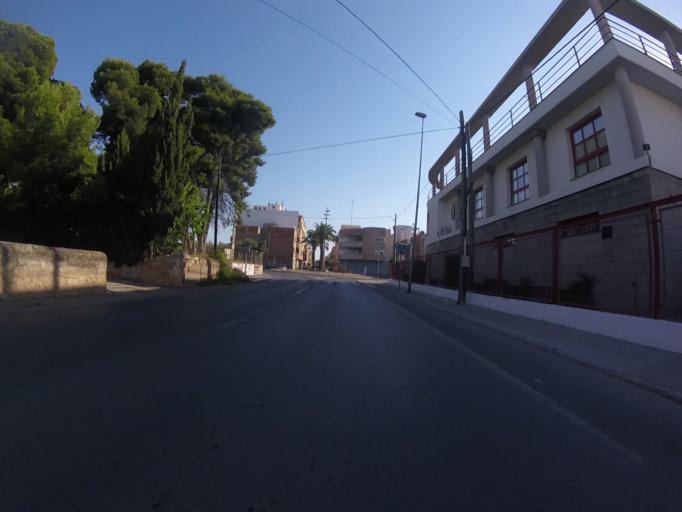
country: ES
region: Valencia
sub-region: Provincia de Castello
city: Benicarlo
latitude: 40.4125
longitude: 0.4222
